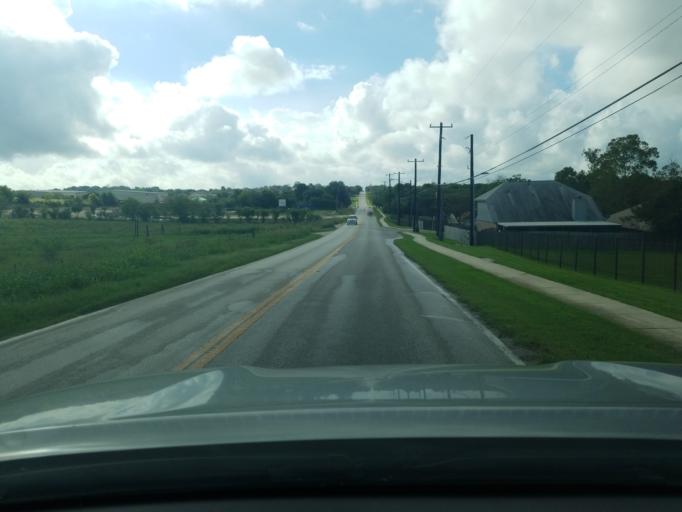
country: US
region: Texas
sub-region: Bexar County
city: Live Oak
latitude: 29.5811
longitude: -98.3640
